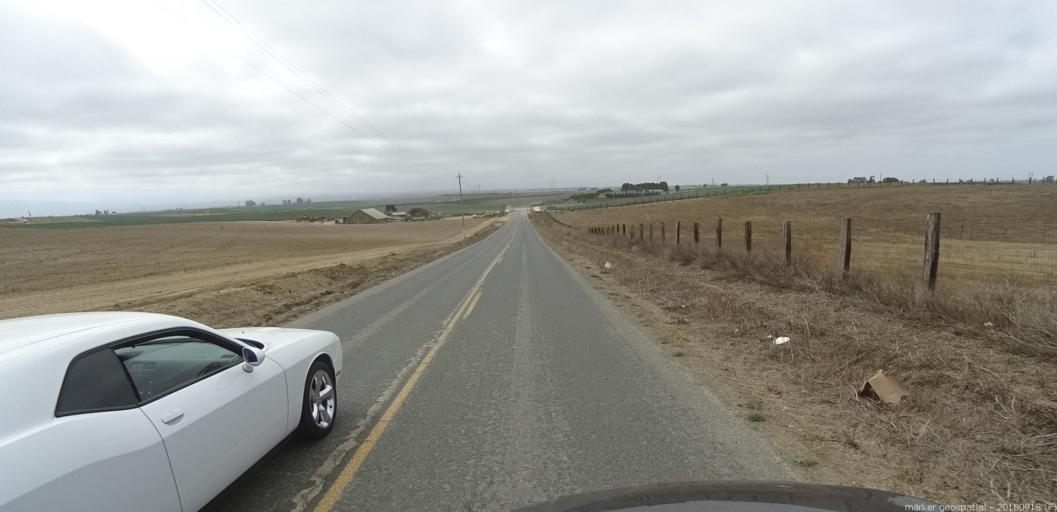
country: US
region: California
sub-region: Monterey County
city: Castroville
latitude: 36.7705
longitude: -121.7219
